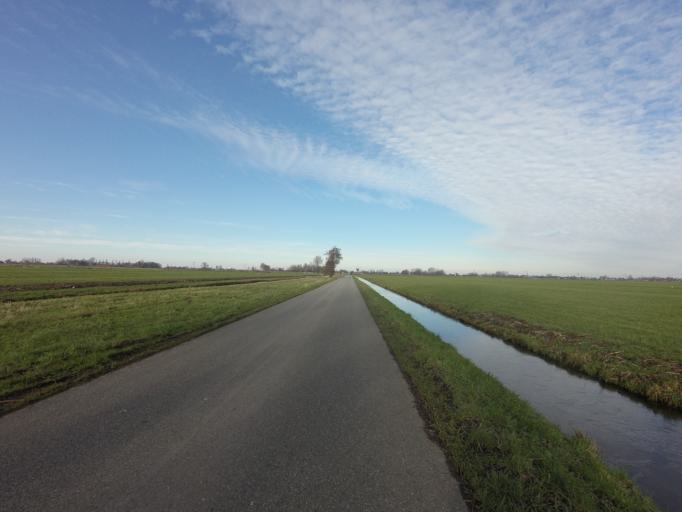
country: NL
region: South Holland
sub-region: Bodegraven-Reeuwijk
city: Bodegraven
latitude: 52.0724
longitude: 4.7923
